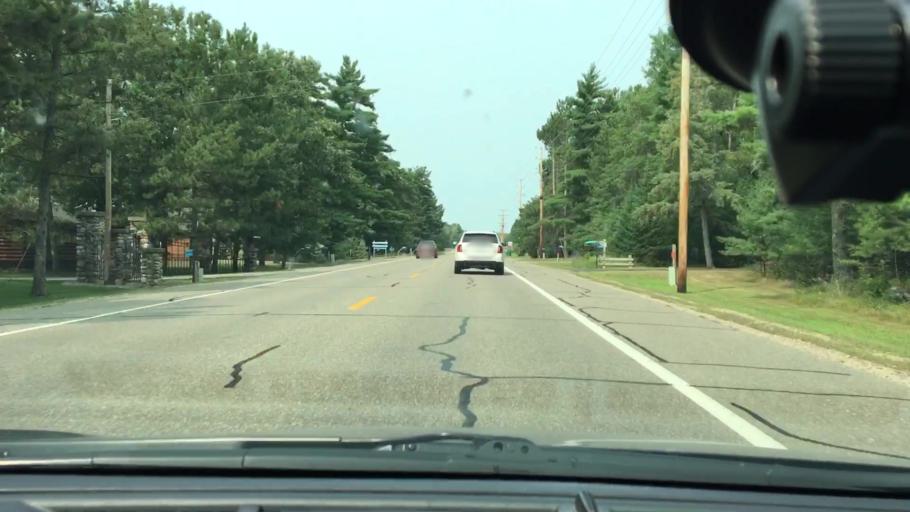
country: US
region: Minnesota
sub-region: Crow Wing County
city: Cross Lake
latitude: 46.5891
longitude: -94.1315
